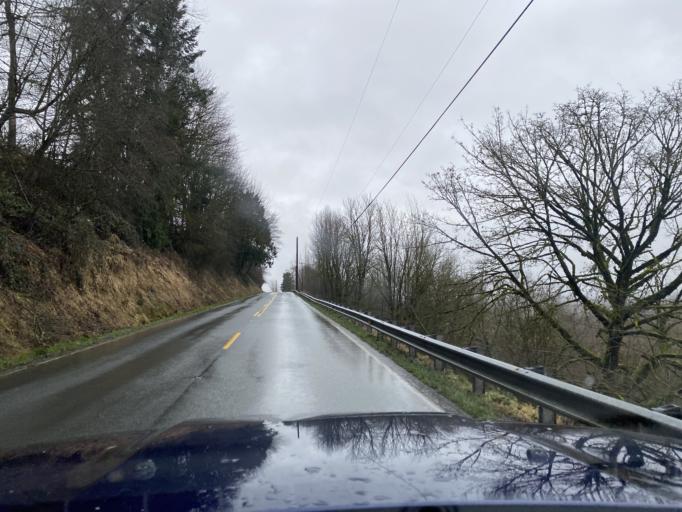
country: US
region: Washington
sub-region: King County
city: Duvall
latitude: 47.7805
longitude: -121.9986
